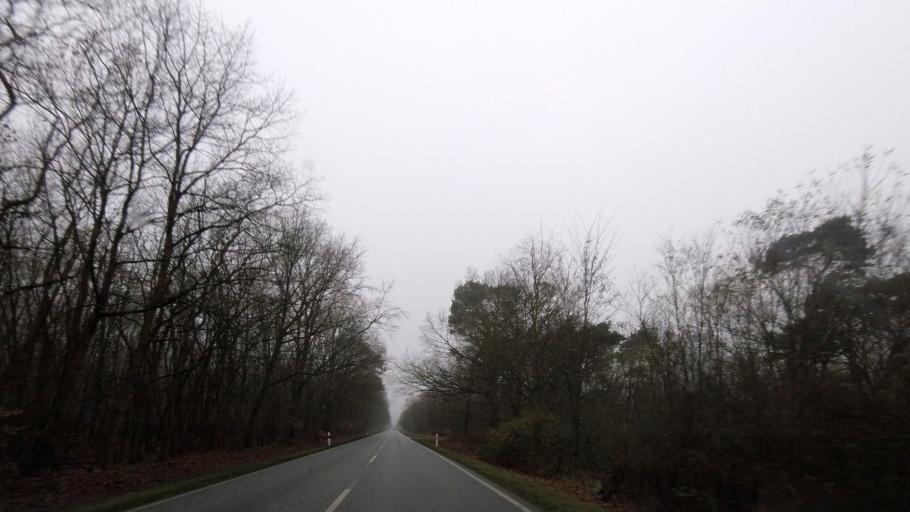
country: DE
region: Brandenburg
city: Niedergorsdorf
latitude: 52.0253
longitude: 12.9757
